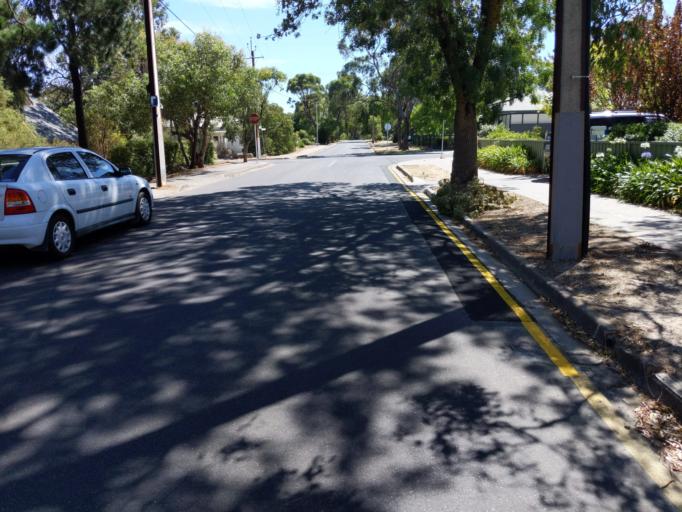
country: AU
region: South Australia
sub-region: Mitcham
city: Blackwood
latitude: -35.0215
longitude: 138.6062
